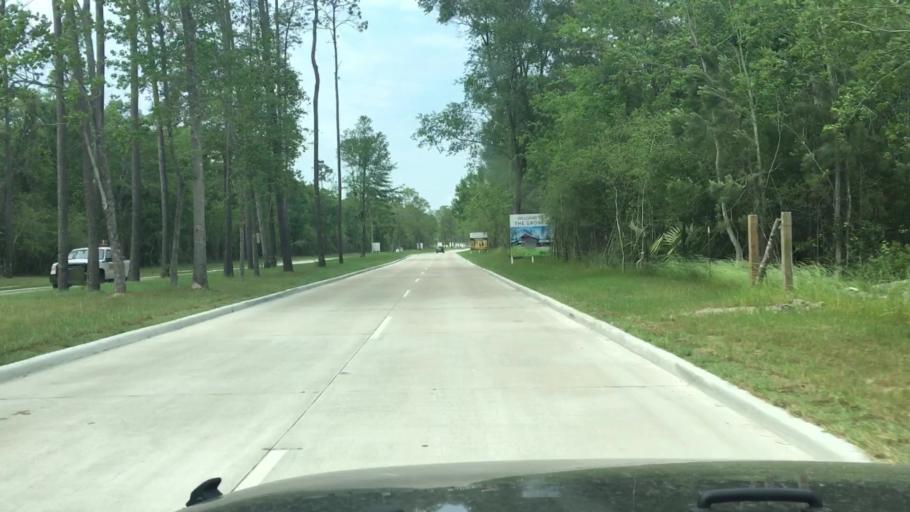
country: US
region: Texas
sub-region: Harris County
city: Atascocita
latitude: 29.9538
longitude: -95.2102
